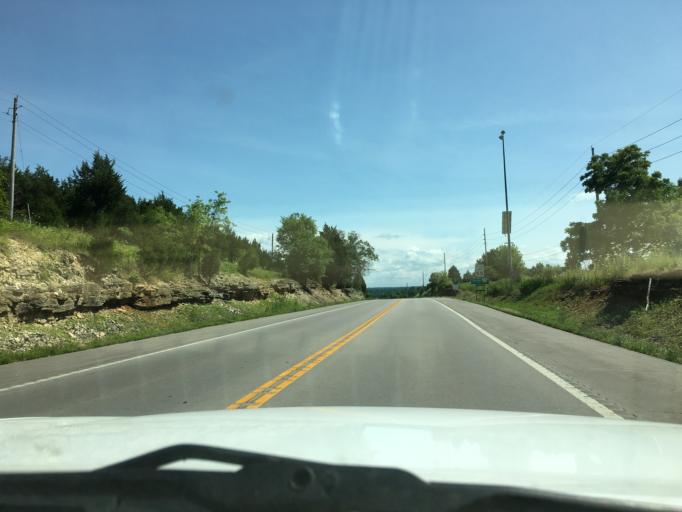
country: US
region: Missouri
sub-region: Franklin County
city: Union
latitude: 38.4733
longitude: -91.0058
